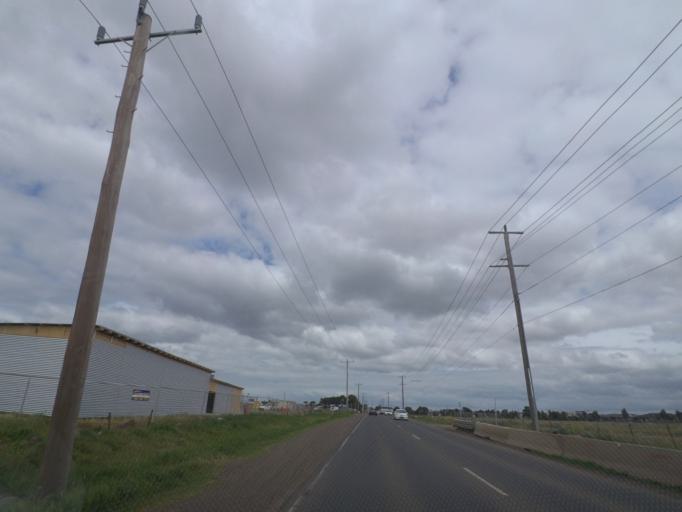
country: AU
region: Victoria
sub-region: Wyndham
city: Williams Landing
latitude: -37.8493
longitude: 144.7457
